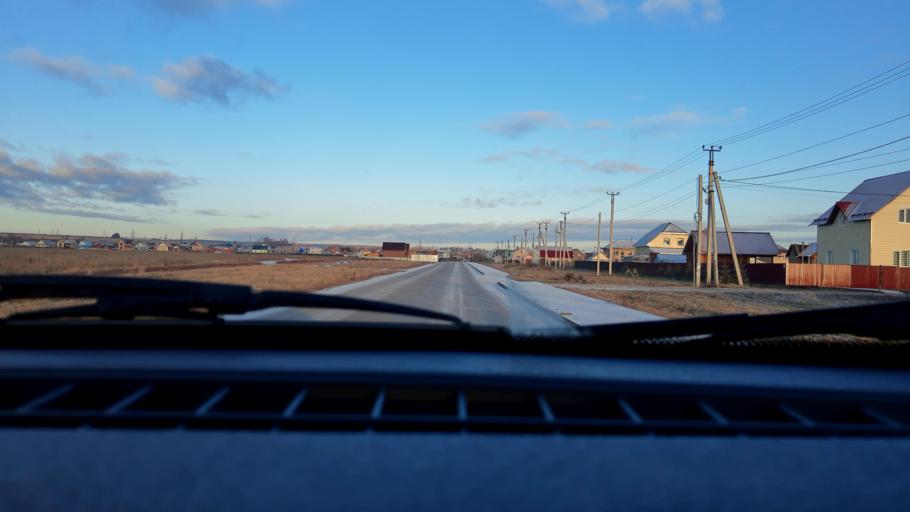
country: RU
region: Bashkortostan
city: Mikhaylovka
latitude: 54.7856
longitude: 55.8323
